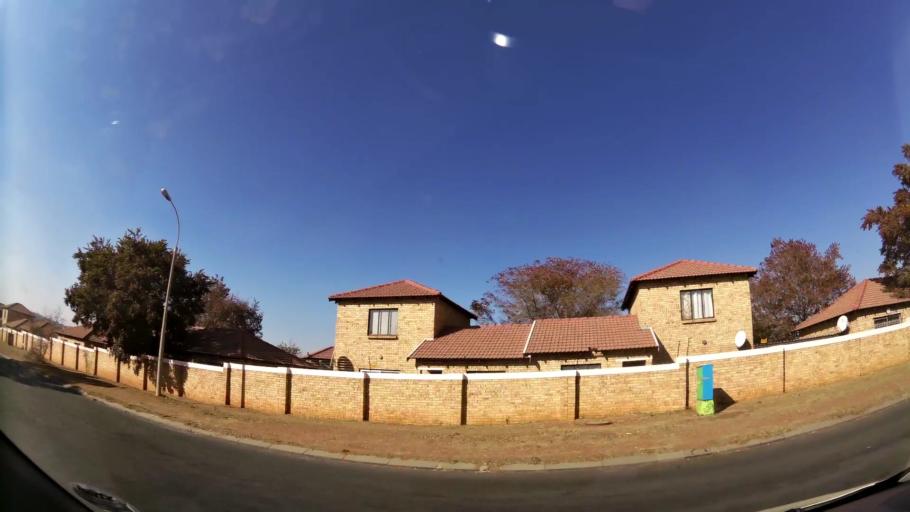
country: ZA
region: Gauteng
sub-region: City of Johannesburg Metropolitan Municipality
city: Roodepoort
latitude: -26.1653
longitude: 27.8248
